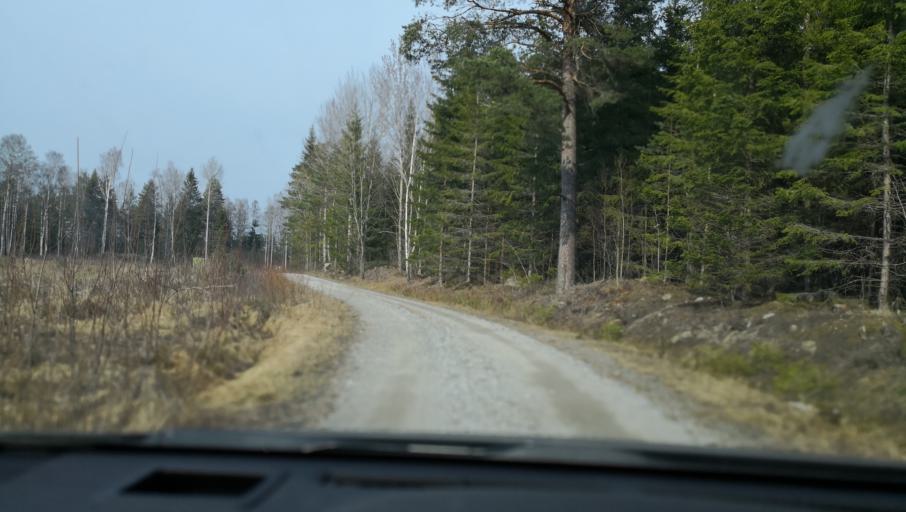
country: SE
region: OErebro
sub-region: Lindesbergs Kommun
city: Frovi
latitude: 59.3880
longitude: 15.4032
